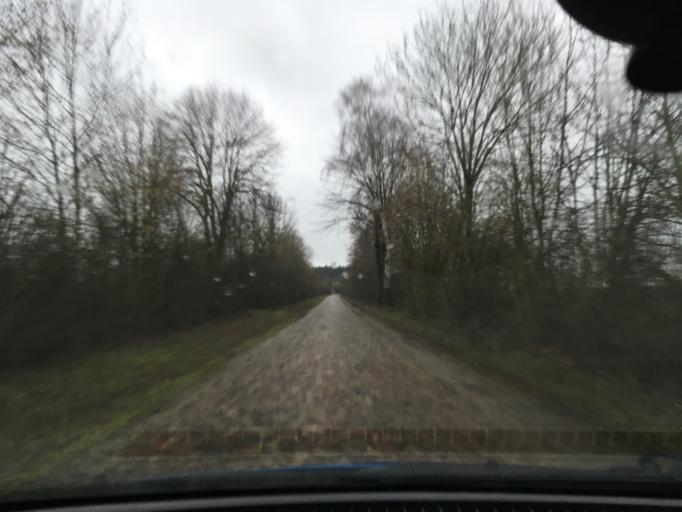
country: DE
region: Schleswig-Holstein
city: Kruzen
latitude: 53.4195
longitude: 10.5328
